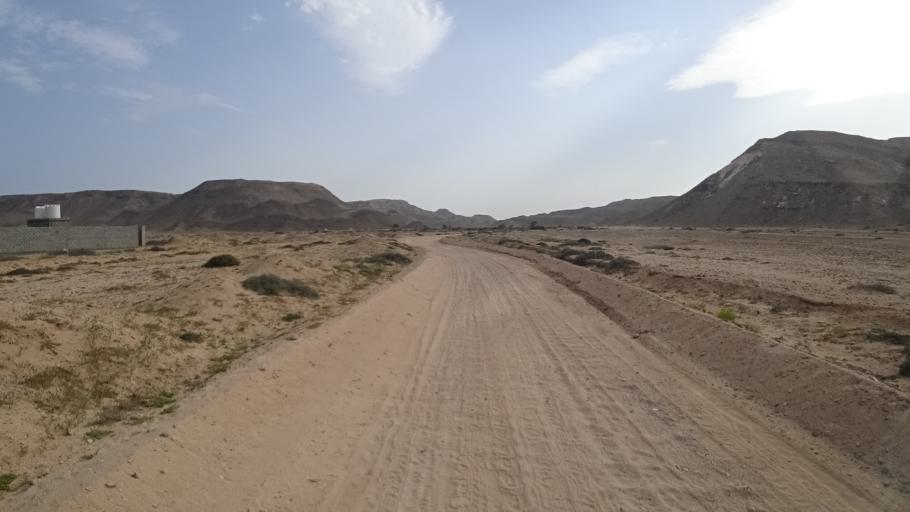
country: OM
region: Ash Sharqiyah
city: Sur
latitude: 22.4387
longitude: 59.8196
